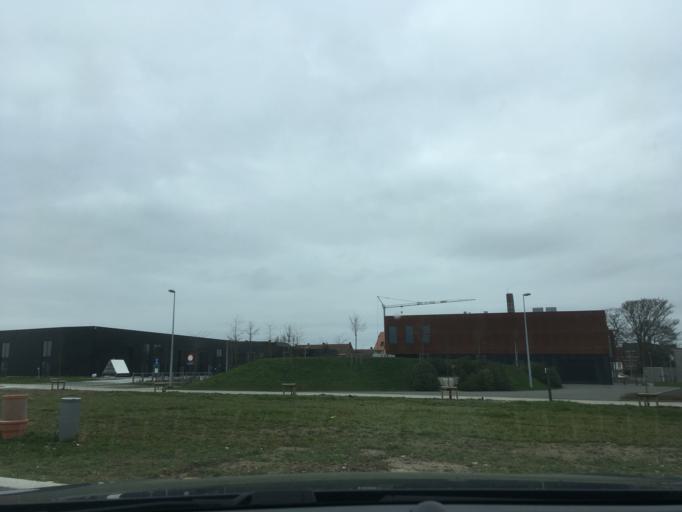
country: BE
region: Flanders
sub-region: Provincie West-Vlaanderen
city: Lichtervelde
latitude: 51.0237
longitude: 3.1360
